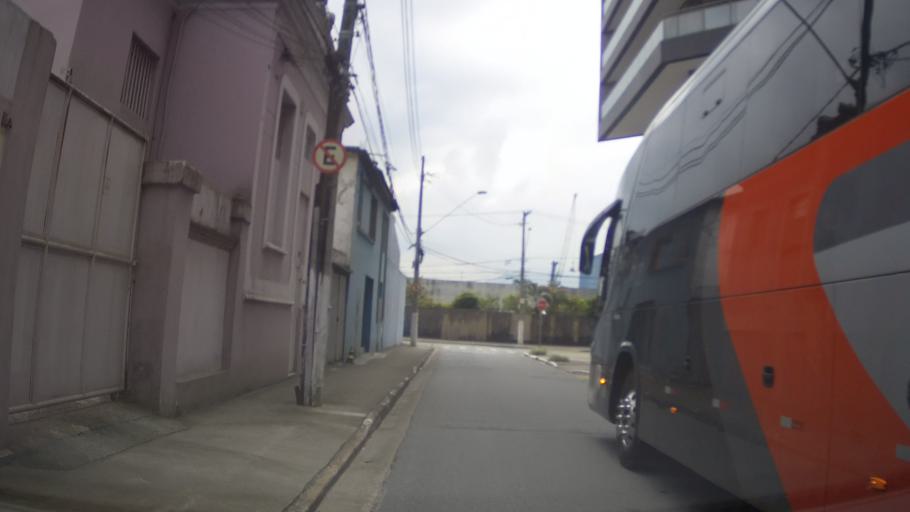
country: BR
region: Sao Paulo
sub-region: Santos
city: Santos
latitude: -23.9308
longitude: -46.3381
